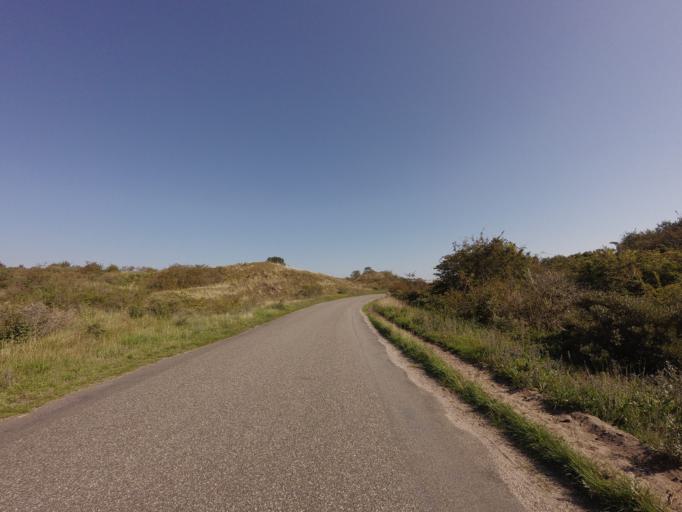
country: NL
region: Friesland
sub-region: Gemeente Schiermonnikoog
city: Schiermonnikoog
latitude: 53.4873
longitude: 6.1798
